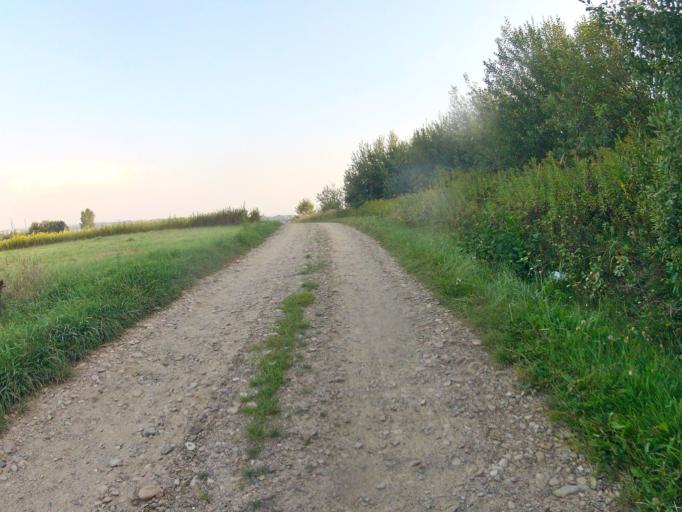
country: PL
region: Subcarpathian Voivodeship
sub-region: Powiat jasielski
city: Brzyska
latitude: 49.7876
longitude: 21.3871
